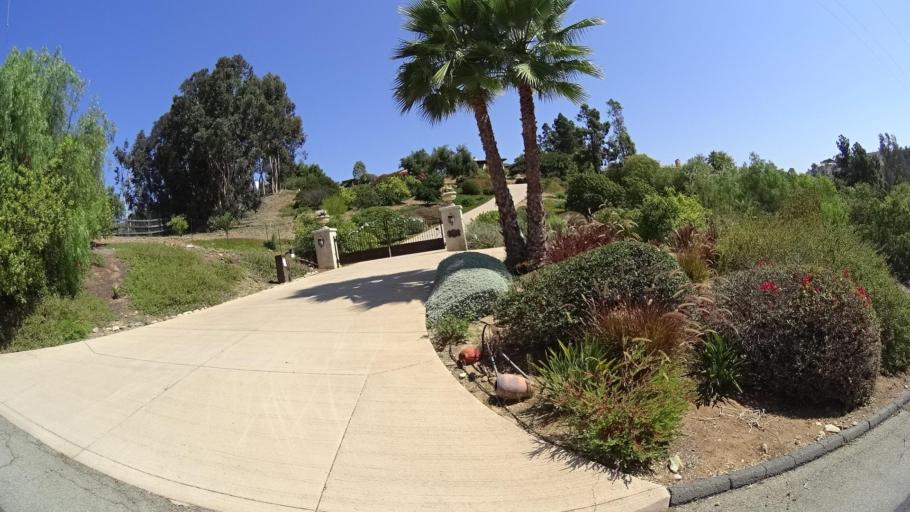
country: US
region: California
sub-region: San Diego County
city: Fairbanks Ranch
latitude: 33.0131
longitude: -117.1778
